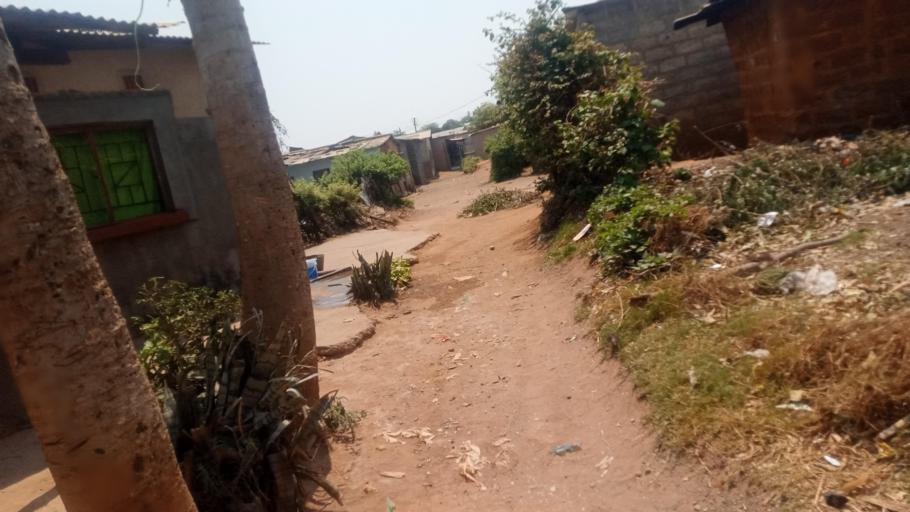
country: ZM
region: Lusaka
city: Lusaka
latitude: -15.4458
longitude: 28.3846
